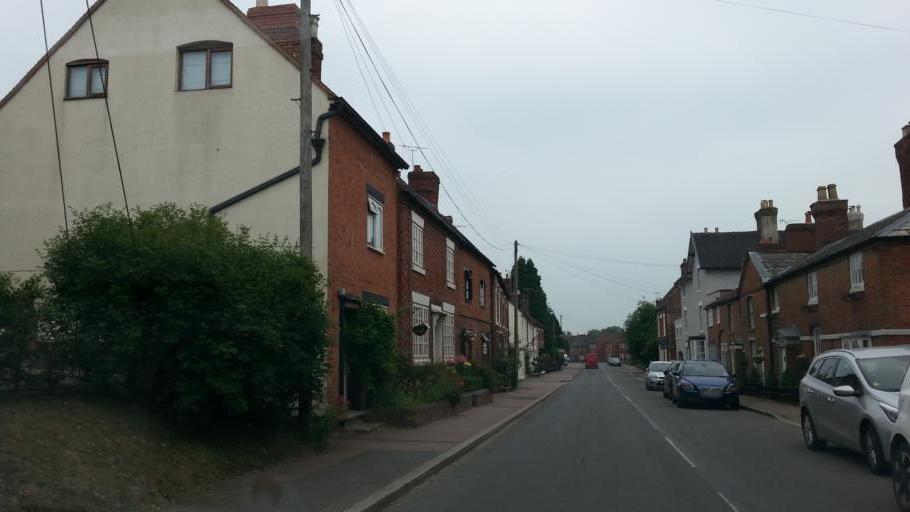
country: GB
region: England
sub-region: Staffordshire
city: Rugeley
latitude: 52.8205
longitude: -1.8885
